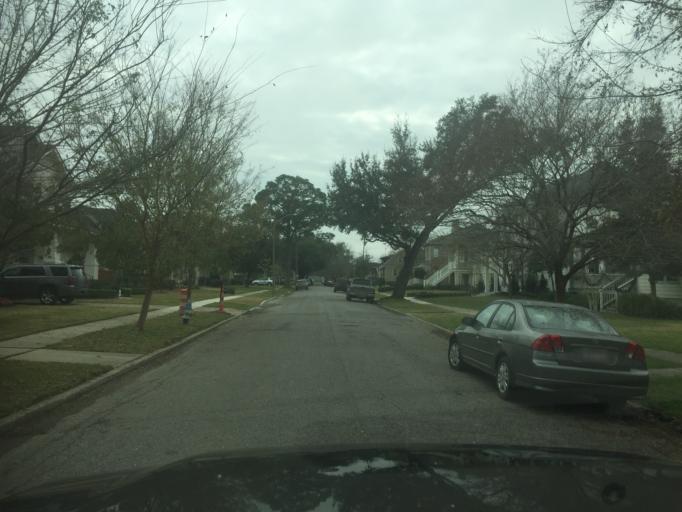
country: US
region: Louisiana
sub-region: Jefferson Parish
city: Metairie
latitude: 29.9982
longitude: -90.1056
